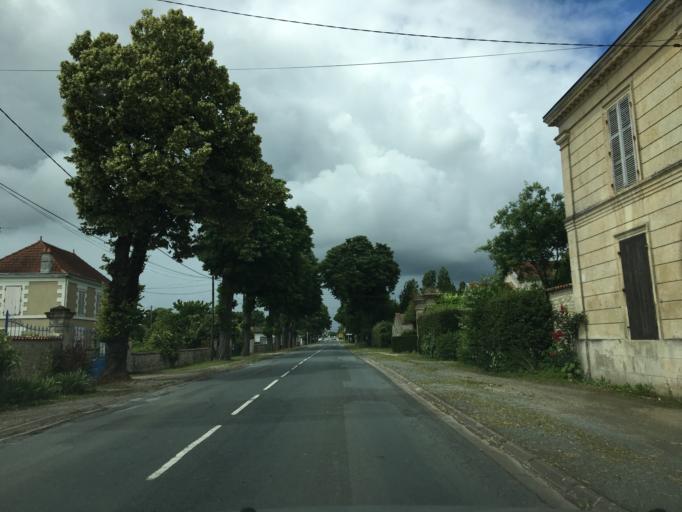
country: FR
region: Poitou-Charentes
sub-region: Departement des Deux-Sevres
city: Beauvoir-sur-Niort
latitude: 46.0936
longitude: -0.5034
